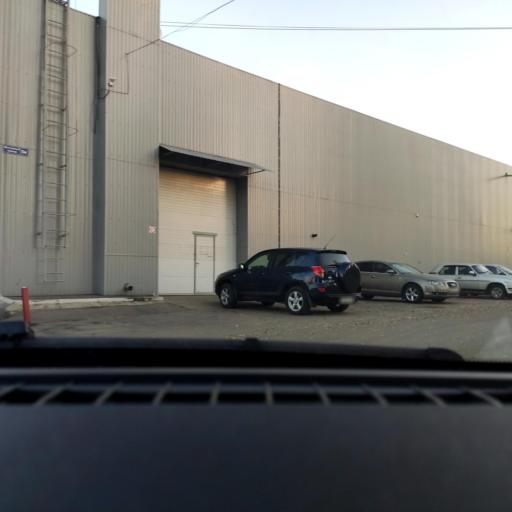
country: RU
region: Voronezj
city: Maslovka
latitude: 51.6393
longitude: 39.2844
